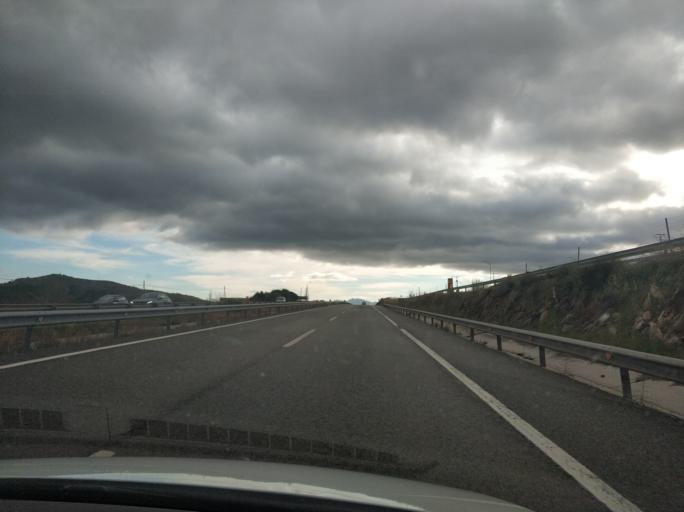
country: ES
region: Madrid
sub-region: Provincia de Madrid
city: Braojos
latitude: 41.0424
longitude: -3.6168
